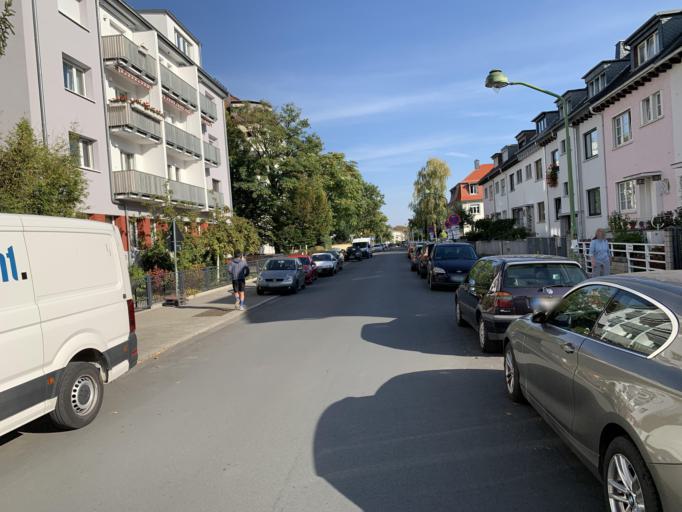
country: DE
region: Hesse
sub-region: Regierungsbezirk Darmstadt
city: Frankfurt am Main
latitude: 50.1225
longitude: 8.7127
